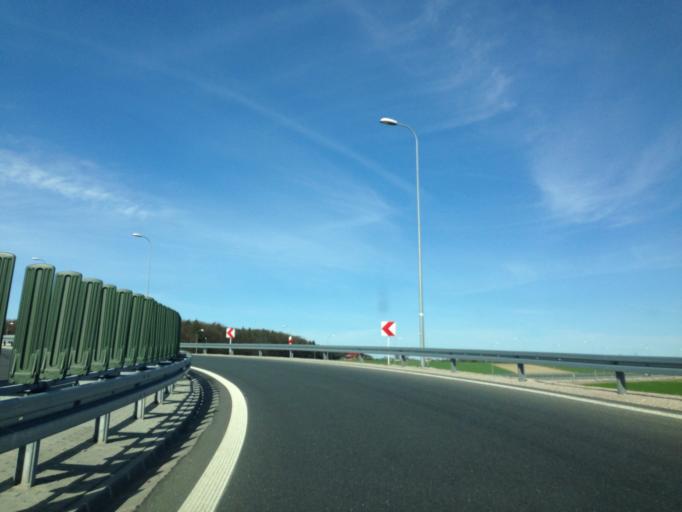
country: PL
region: Lodz Voivodeship
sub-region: Powiat zdunskowolski
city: Zapolice
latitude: 51.5917
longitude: 18.8238
